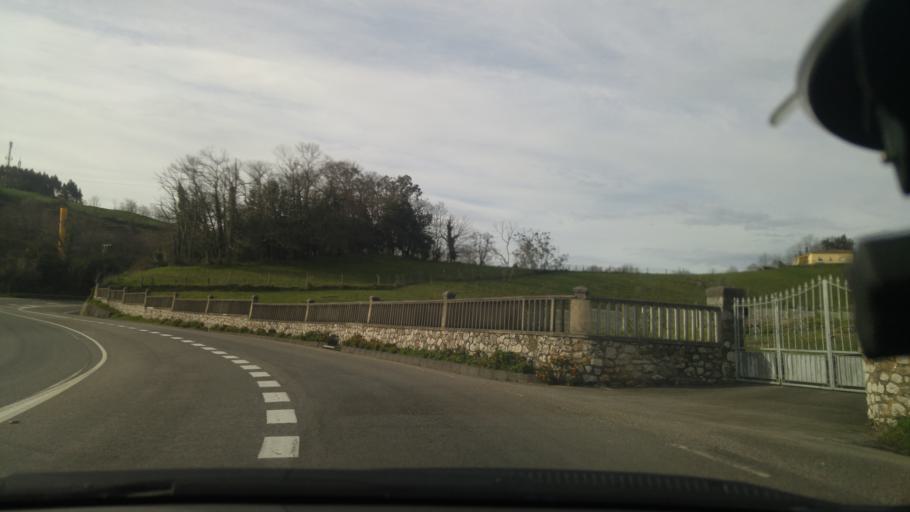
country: ES
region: Asturias
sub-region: Province of Asturias
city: Llanera
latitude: 43.4587
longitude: -5.8505
